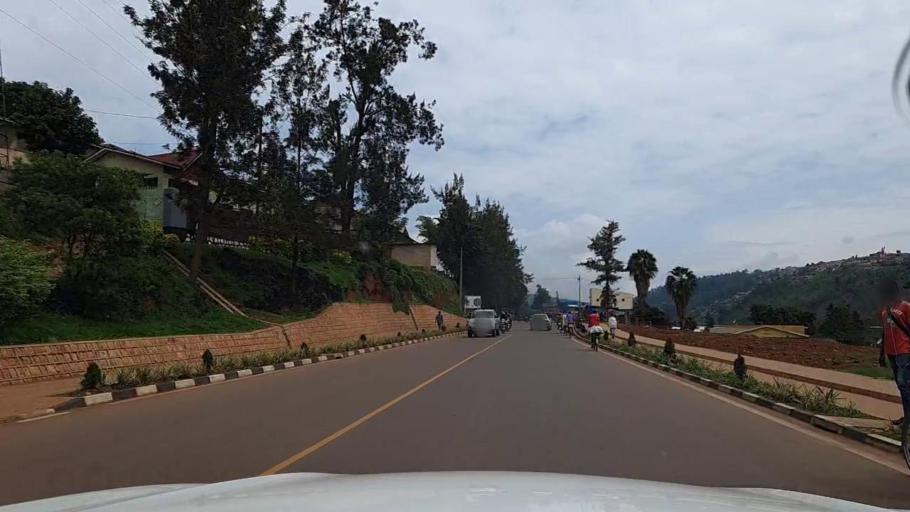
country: RW
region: Kigali
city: Kigali
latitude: -1.9332
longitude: 30.0454
